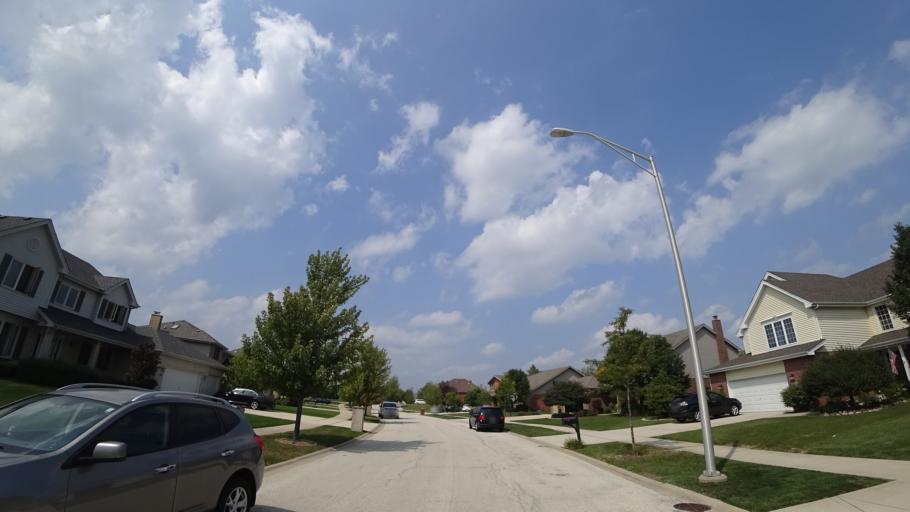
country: US
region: Illinois
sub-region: Will County
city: Goodings Grove
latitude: 41.6343
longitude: -87.9028
